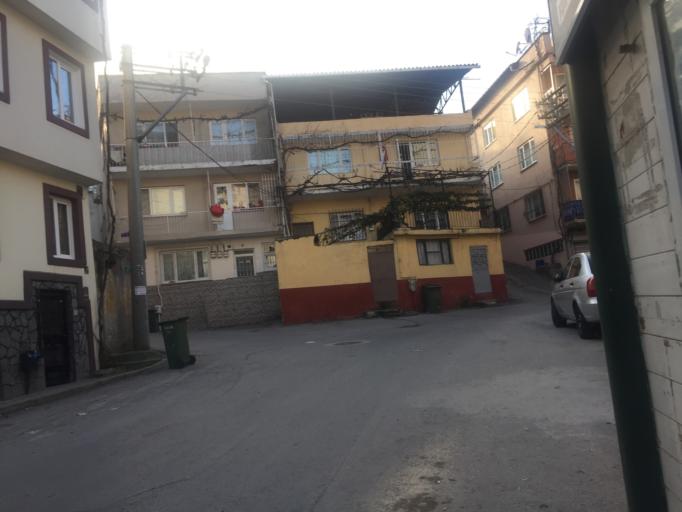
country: TR
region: Bursa
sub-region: Osmangazi
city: Bursa
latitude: 40.1867
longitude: 29.0841
